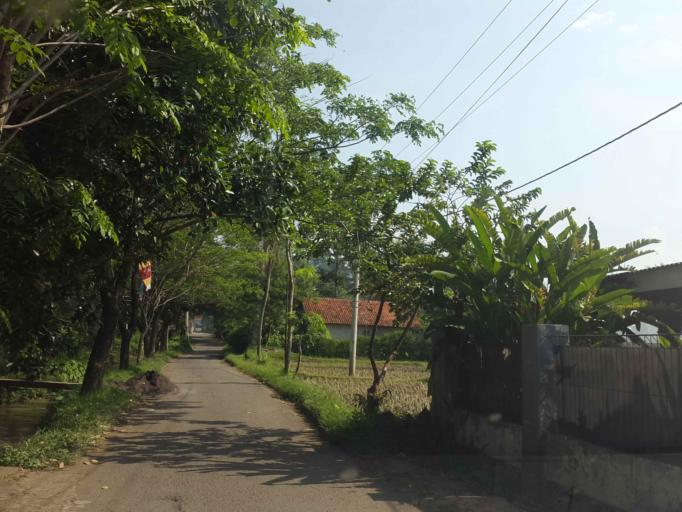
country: ID
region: West Java
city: Ciranjang-hilir
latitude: -6.7837
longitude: 107.2738
